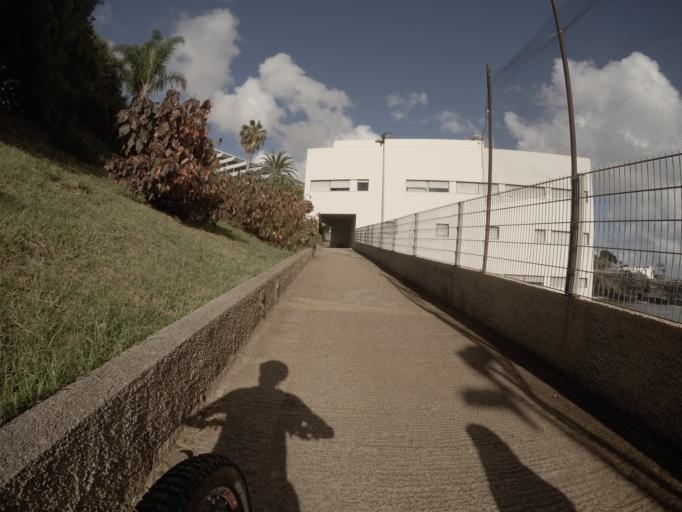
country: PT
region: Madeira
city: Camara de Lobos
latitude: 32.6366
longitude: -16.9359
